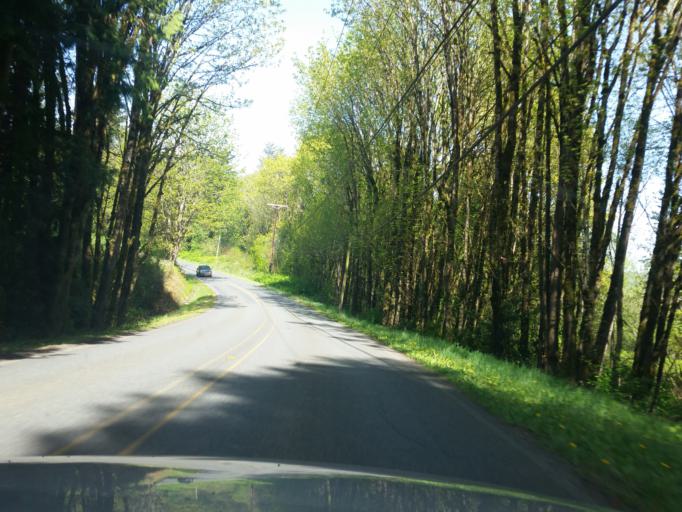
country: US
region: Washington
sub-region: Snohomish County
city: Cathcart
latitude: 47.8760
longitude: -122.1035
